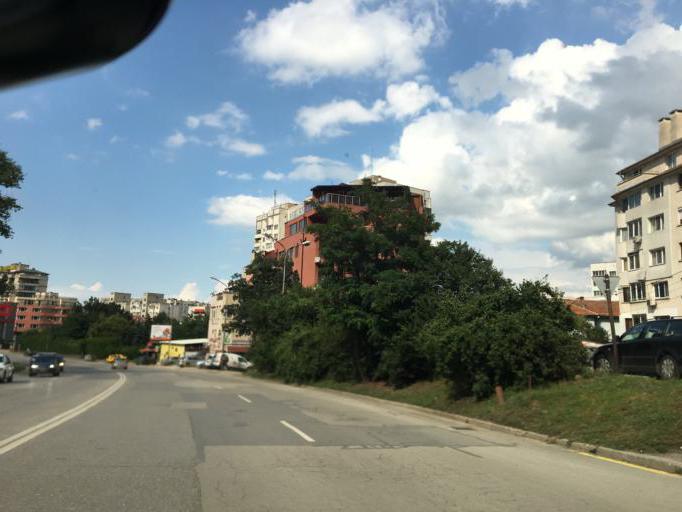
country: BG
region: Sofia-Capital
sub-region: Stolichna Obshtina
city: Sofia
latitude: 42.6519
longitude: 23.3595
